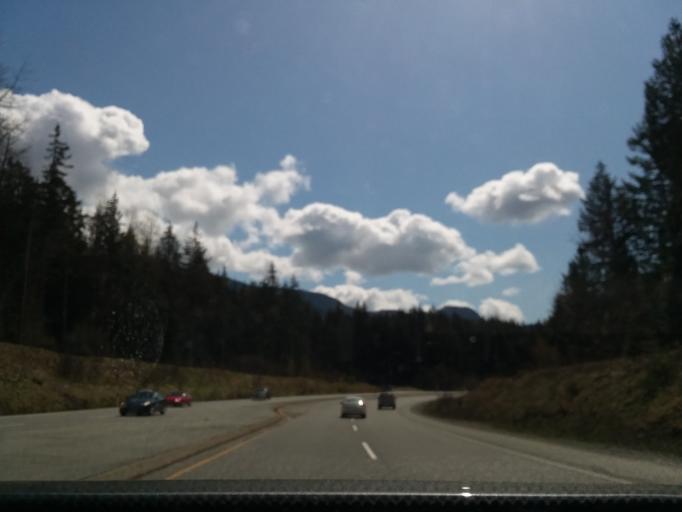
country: CA
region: British Columbia
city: Whistler
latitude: 49.9745
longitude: -123.1434
